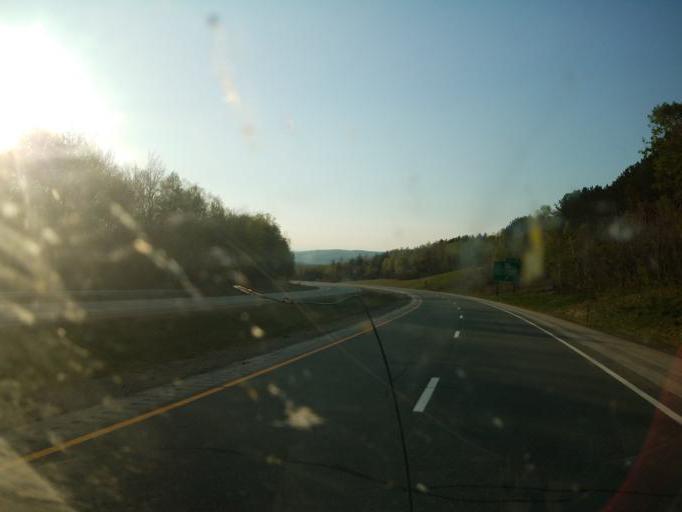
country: US
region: New Hampshire
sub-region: Grafton County
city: Deerfield
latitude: 44.1994
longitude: -71.6818
